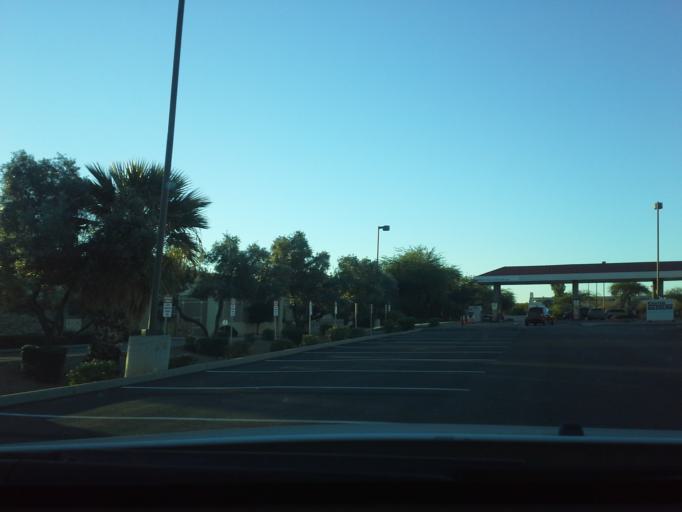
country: US
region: Arizona
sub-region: Maricopa County
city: Guadalupe
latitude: 33.3479
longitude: -111.9610
